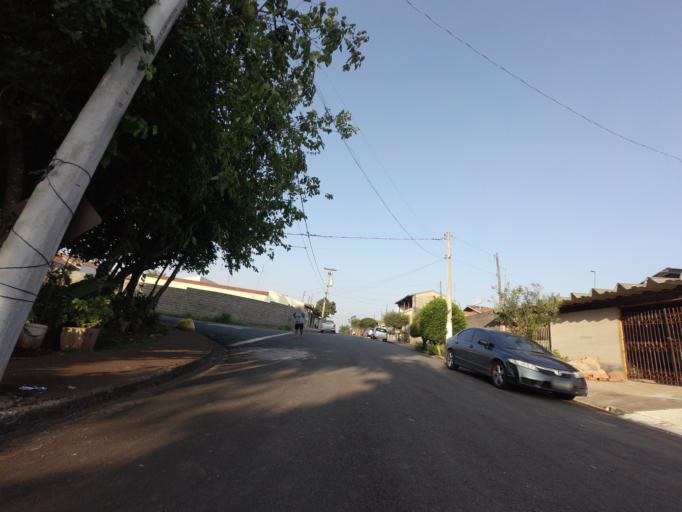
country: BR
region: Sao Paulo
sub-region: Piracicaba
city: Piracicaba
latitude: -22.7503
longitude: -47.6015
